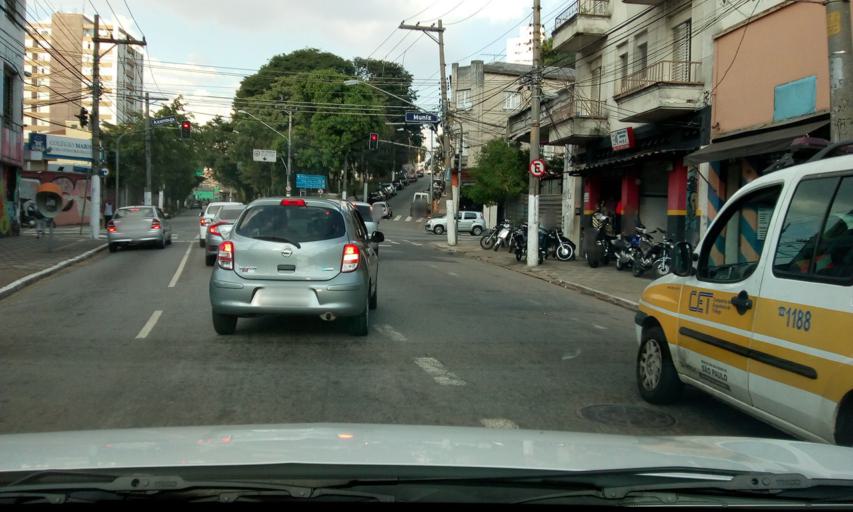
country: BR
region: Sao Paulo
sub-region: Sao Paulo
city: Sao Paulo
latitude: -23.5620
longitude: -46.6244
